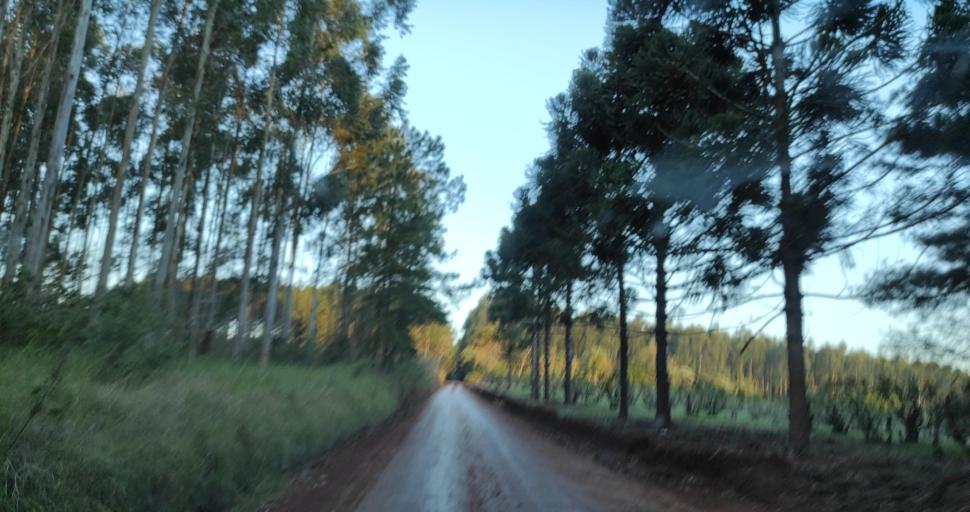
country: AR
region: Misiones
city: Capiovi
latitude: -26.8844
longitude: -55.0841
